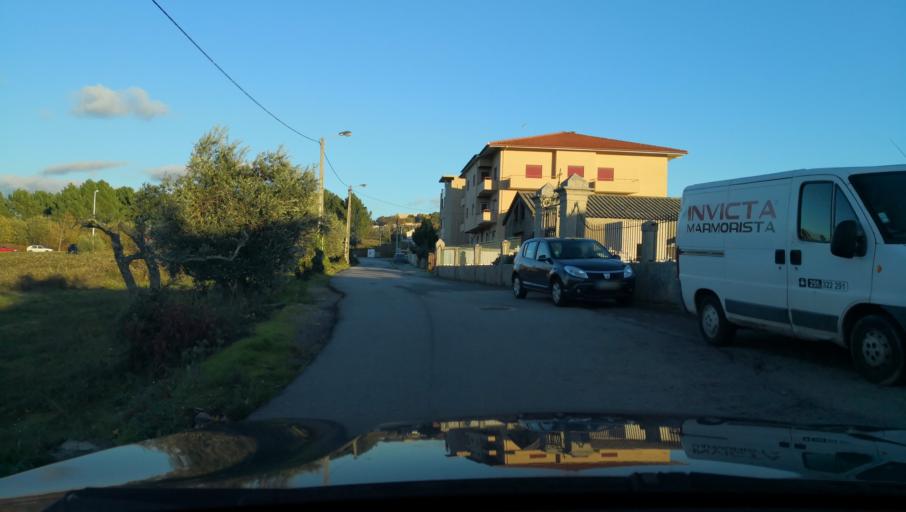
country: PT
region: Vila Real
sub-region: Vila Real
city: Vila Real
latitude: 41.2804
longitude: -7.7387
